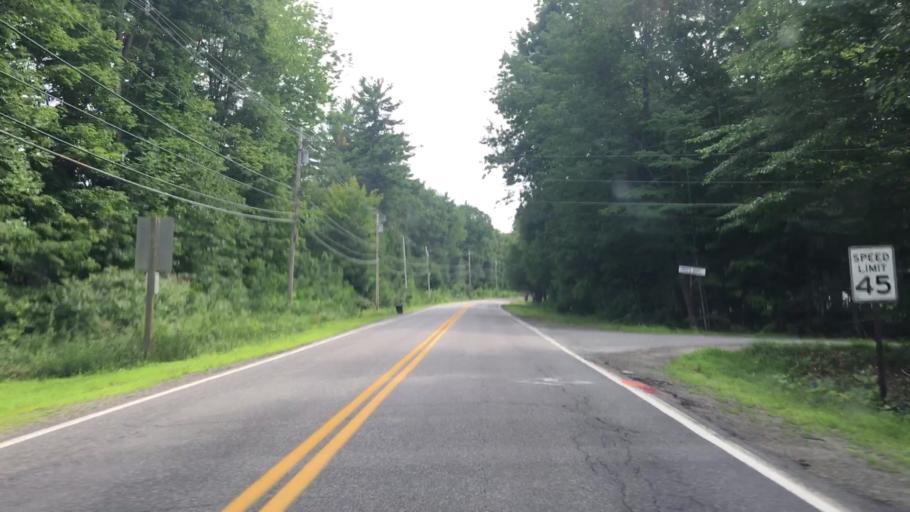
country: US
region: Maine
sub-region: Kennebec County
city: Winslow
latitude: 44.5216
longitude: -69.6309
